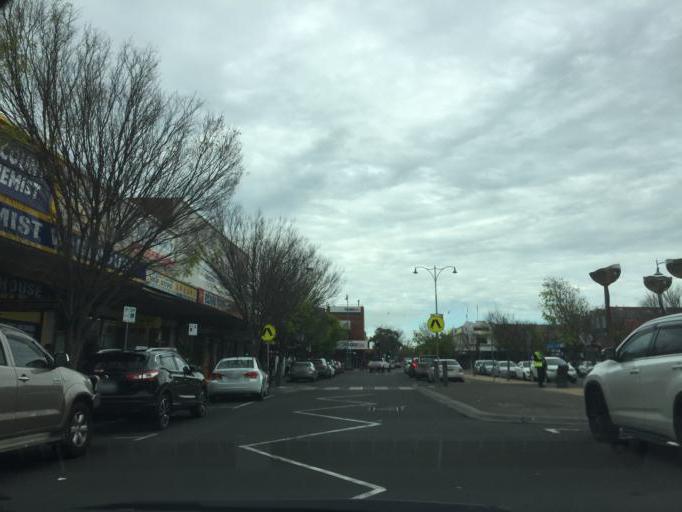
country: AU
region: Victoria
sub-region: Brimbank
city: Sunshine North
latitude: -37.7839
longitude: 144.8324
